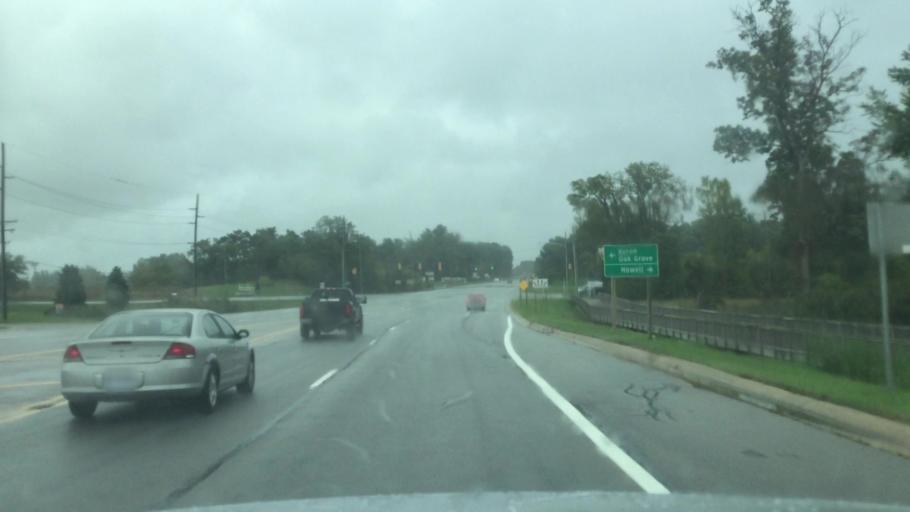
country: US
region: Michigan
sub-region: Livingston County
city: Howell
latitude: 42.6225
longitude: -83.9275
